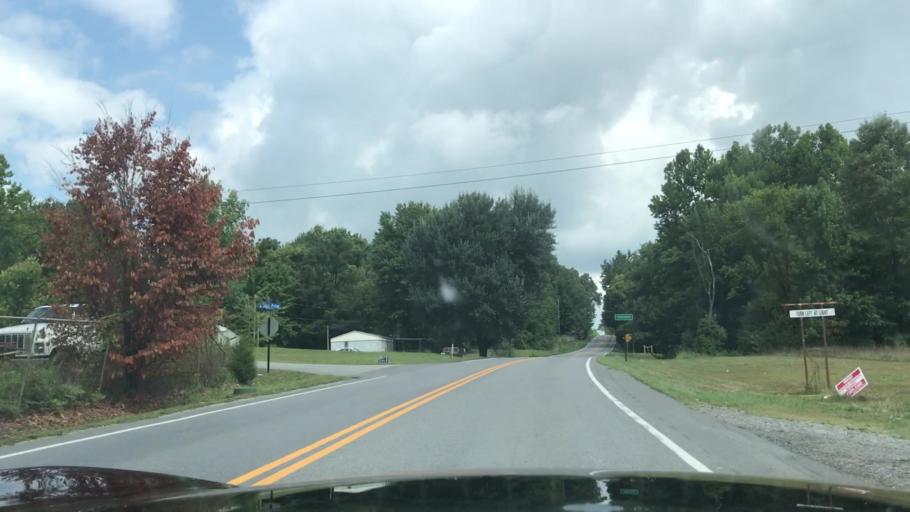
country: US
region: Kentucky
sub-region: Muhlenberg County
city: Central City
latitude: 37.2137
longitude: -87.0447
